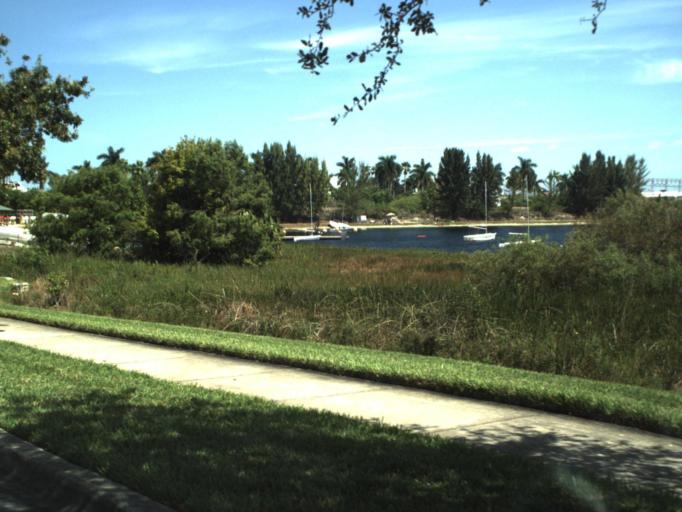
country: US
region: Florida
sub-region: Broward County
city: Dania Beach
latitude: 26.0603
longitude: -80.1679
